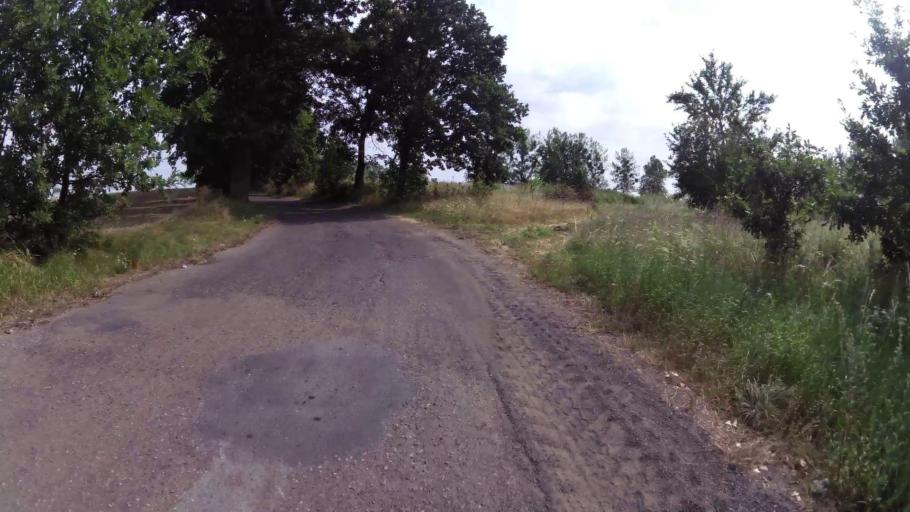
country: PL
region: West Pomeranian Voivodeship
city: Trzcinsko Zdroj
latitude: 52.9302
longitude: 14.6643
